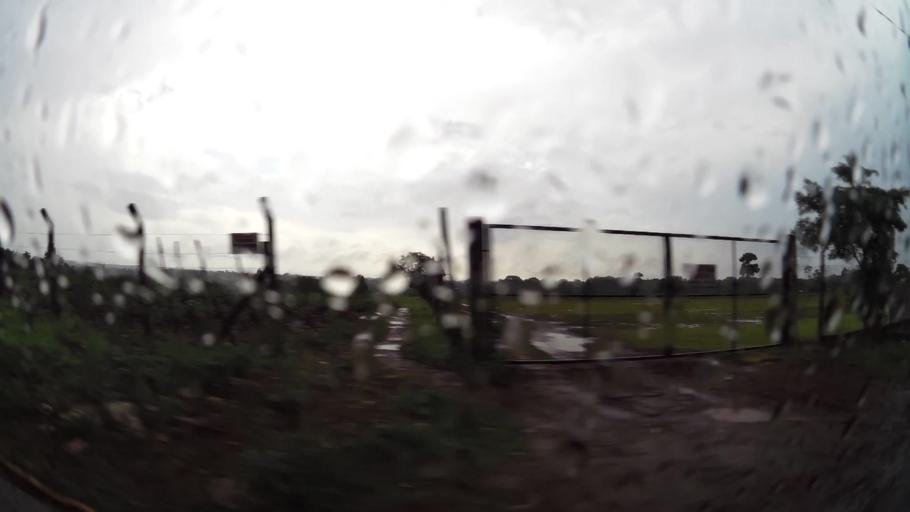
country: PY
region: Alto Parana
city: Presidente Franco
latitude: -25.5417
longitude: -54.6784
